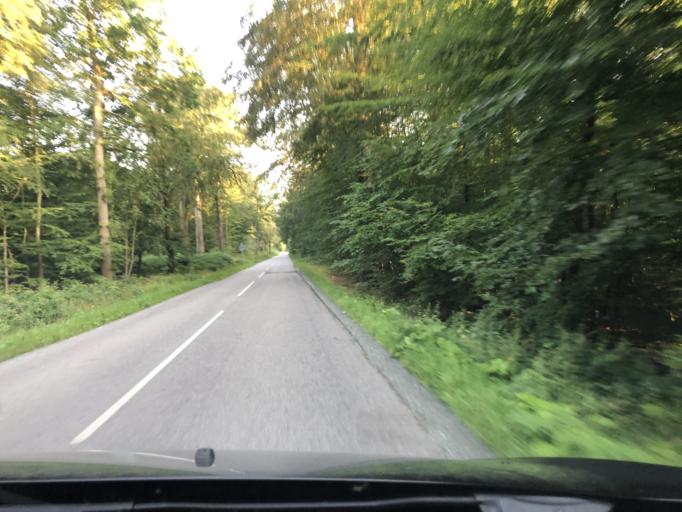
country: DK
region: South Denmark
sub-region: Vejle Kommune
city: Borkop
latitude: 55.6839
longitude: 9.6152
